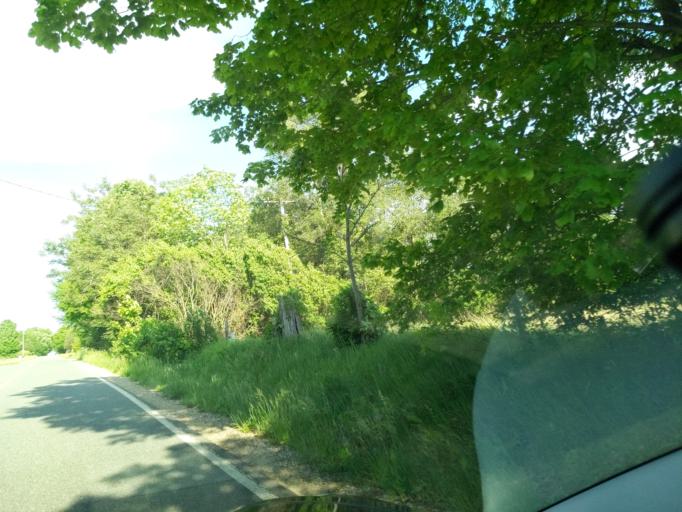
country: US
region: Michigan
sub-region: Barry County
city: Nashville
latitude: 42.6251
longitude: -85.1053
